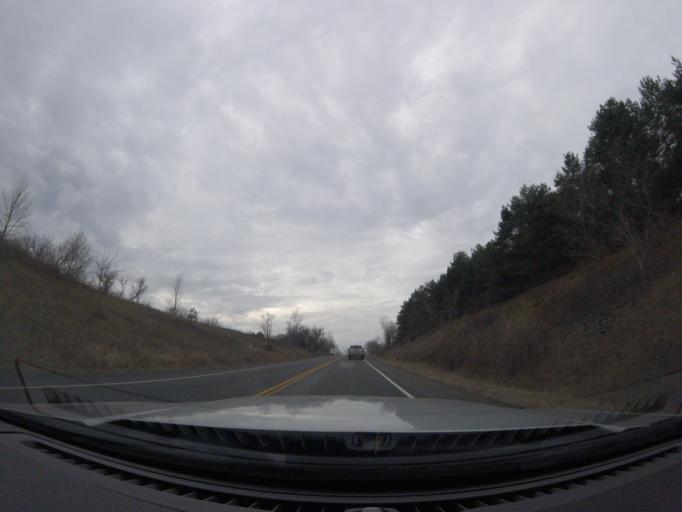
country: US
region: New York
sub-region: Schuyler County
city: Watkins Glen
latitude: 42.4288
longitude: -76.8026
